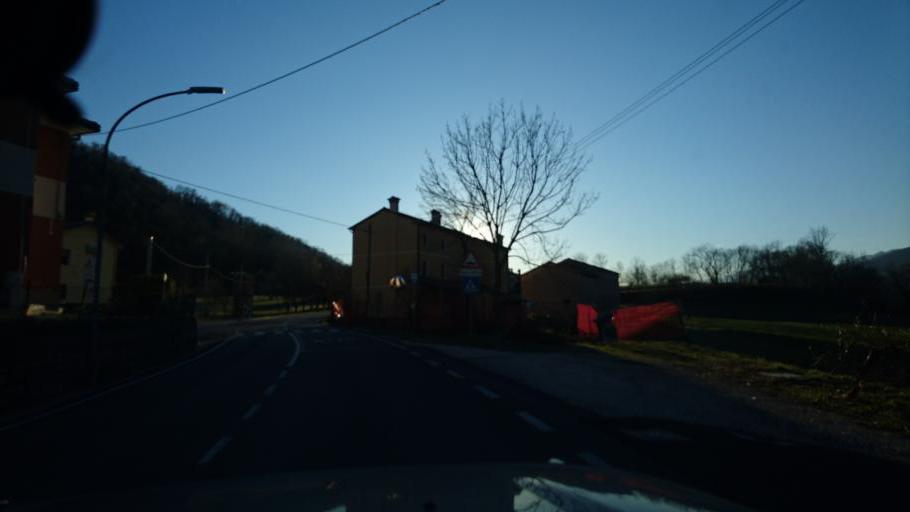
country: IT
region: Veneto
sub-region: Provincia di Treviso
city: Santa Maria
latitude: 45.9880
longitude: 12.2409
